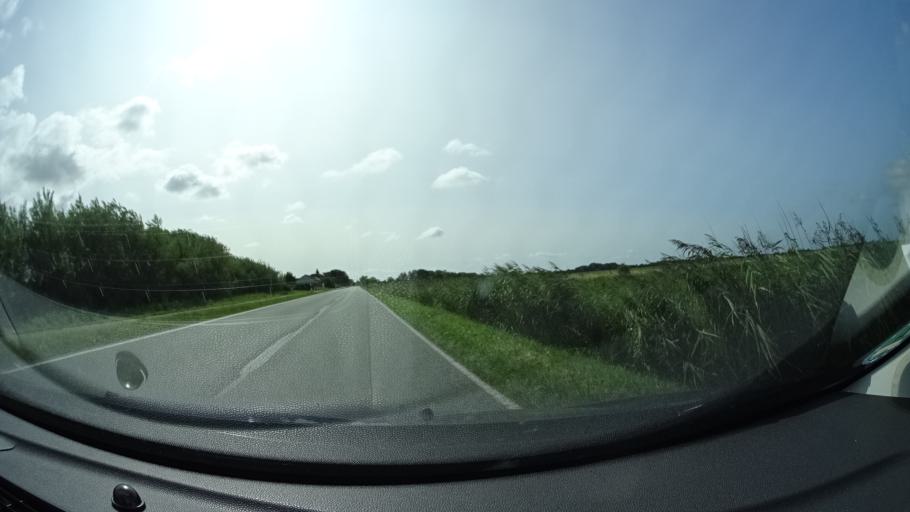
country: DE
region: Schleswig-Holstein
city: Neukirchen
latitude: 54.8818
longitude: 8.7504
